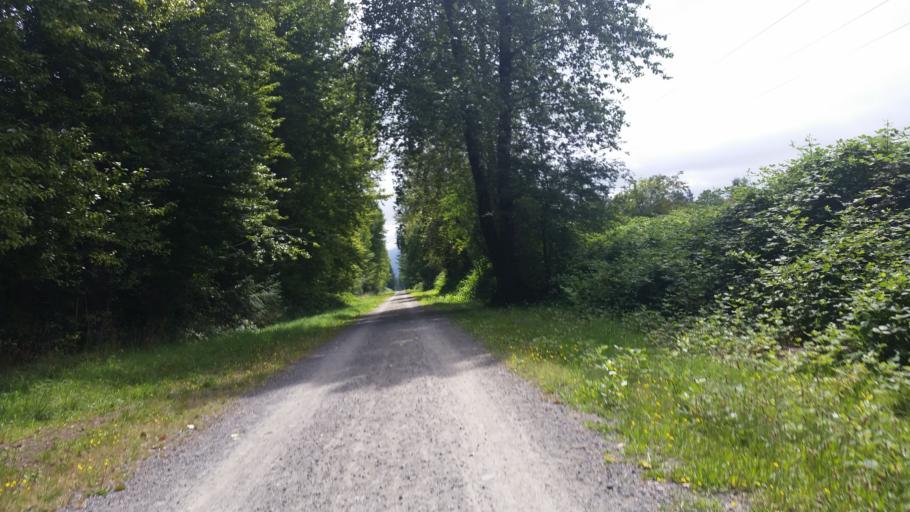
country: US
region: Washington
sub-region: King County
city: North Bend
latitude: 47.4903
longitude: -121.7702
